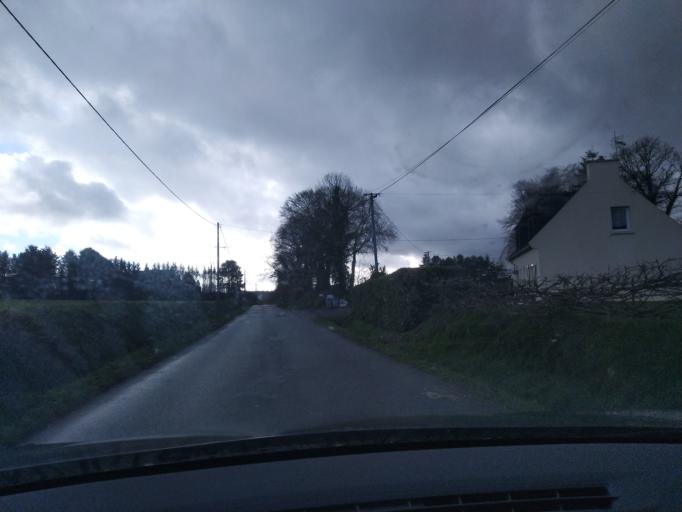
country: FR
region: Brittany
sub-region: Departement du Finistere
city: Guerlesquin
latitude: 48.5112
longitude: -3.5883
